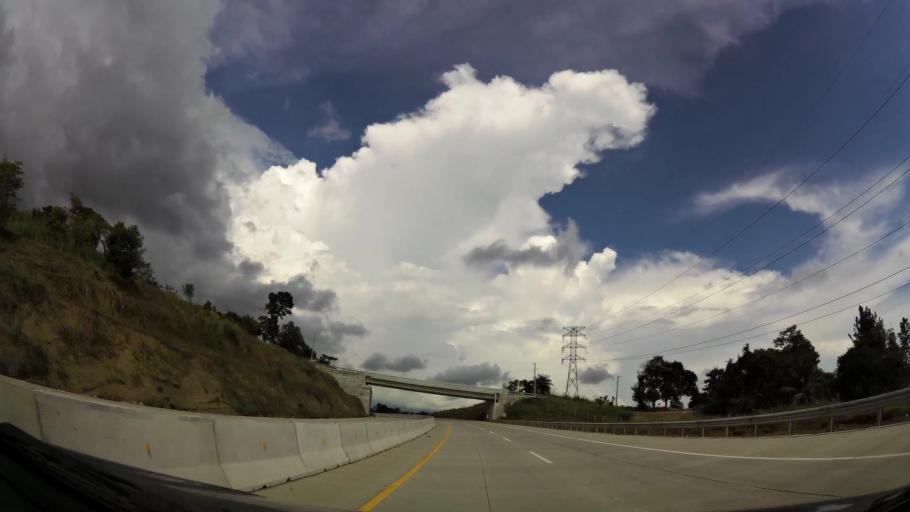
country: PA
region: Panama
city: Tocumen
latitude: 9.0918
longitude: -79.4257
